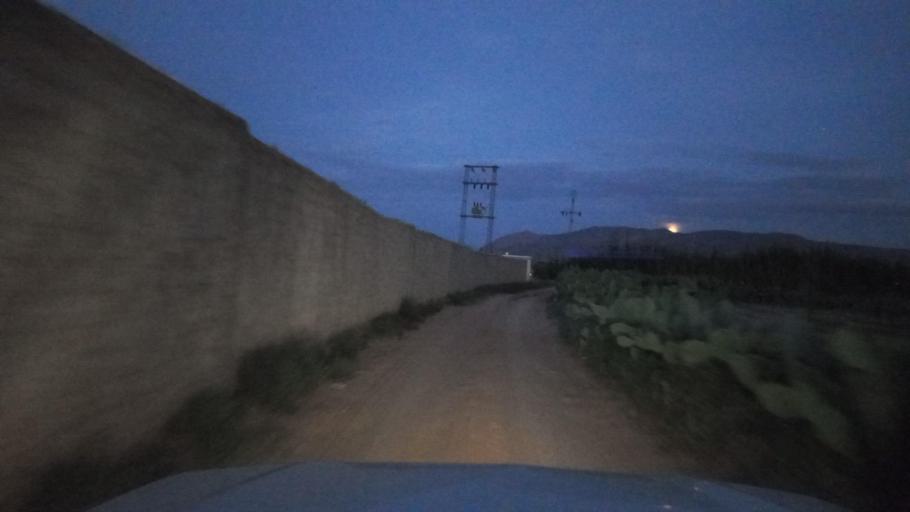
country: TN
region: Al Qasrayn
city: Sbiba
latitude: 35.4206
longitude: 9.1254
